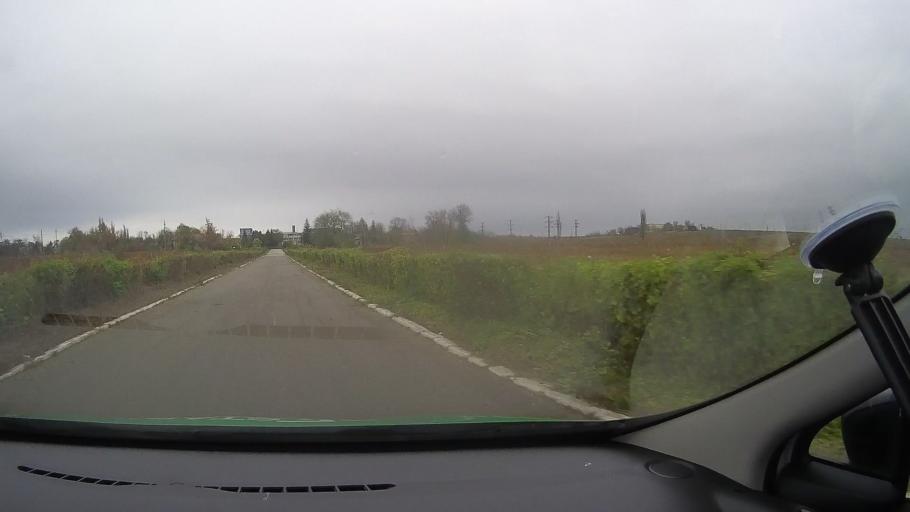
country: RO
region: Constanta
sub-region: Oras Murfatlar
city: Murfatlar
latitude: 44.1745
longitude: 28.4227
